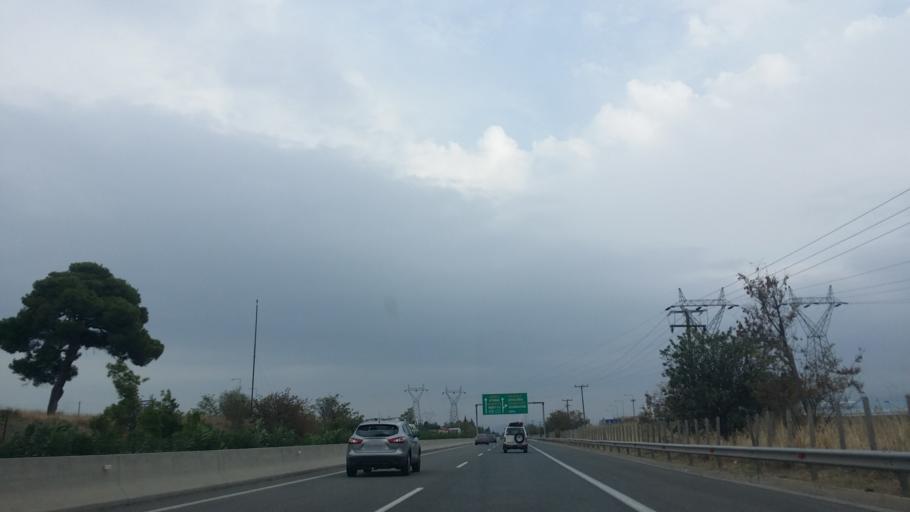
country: GR
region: Central Greece
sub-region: Nomos Voiotias
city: Schimatari
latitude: 38.3596
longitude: 23.5580
